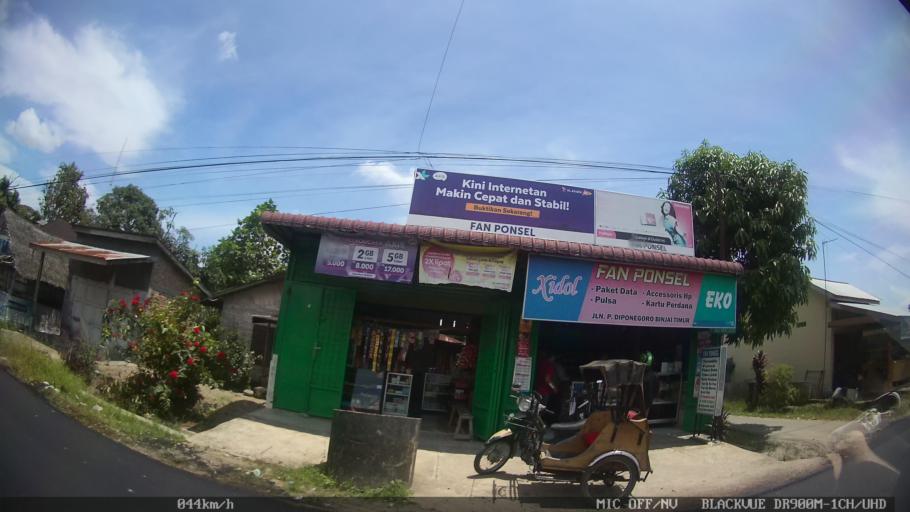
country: ID
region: North Sumatra
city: Binjai
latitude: 3.5913
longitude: 98.4989
